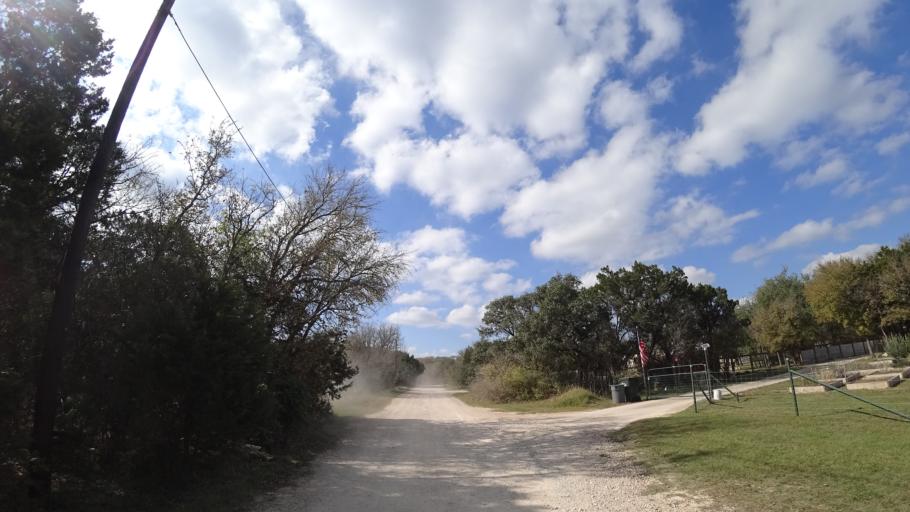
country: US
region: Texas
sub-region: Travis County
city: Shady Hollow
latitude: 30.1738
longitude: -97.8643
